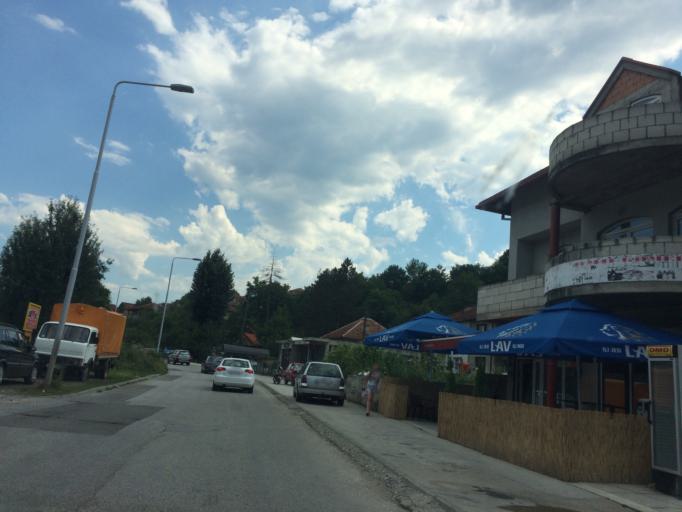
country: RS
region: Central Serbia
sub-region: Zlatiborski Okrug
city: Prijepolje
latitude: 43.3658
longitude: 19.6289
